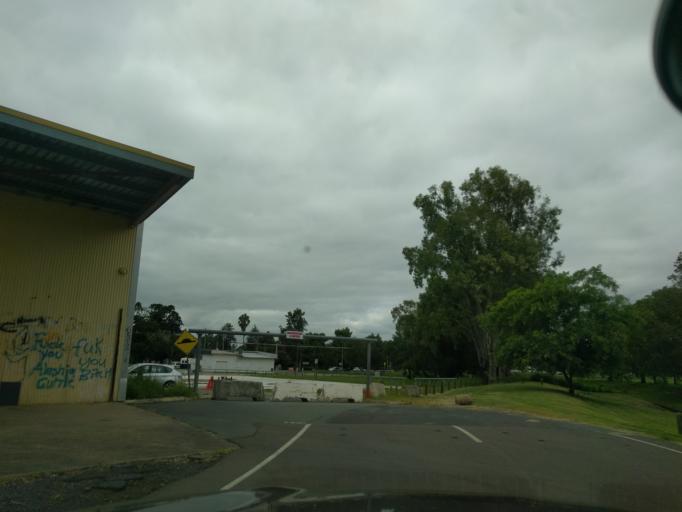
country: AU
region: Queensland
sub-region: Logan
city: Cedar Vale
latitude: -27.9880
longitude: 152.9940
